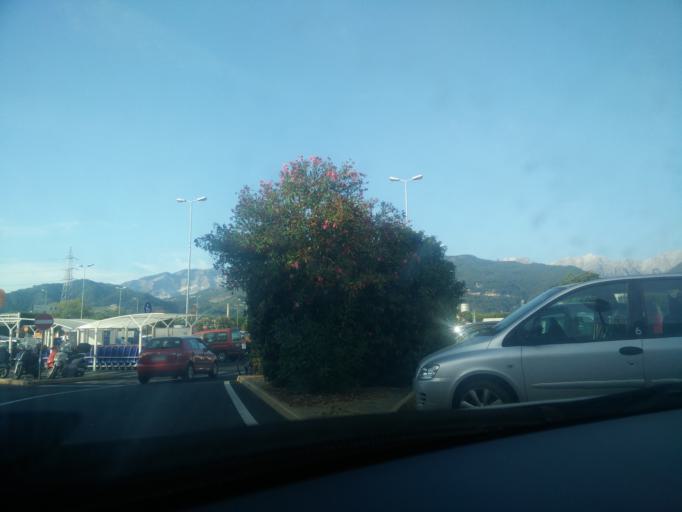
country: IT
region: Tuscany
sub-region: Provincia di Massa-Carrara
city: Massa
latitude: 44.0231
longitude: 10.1095
